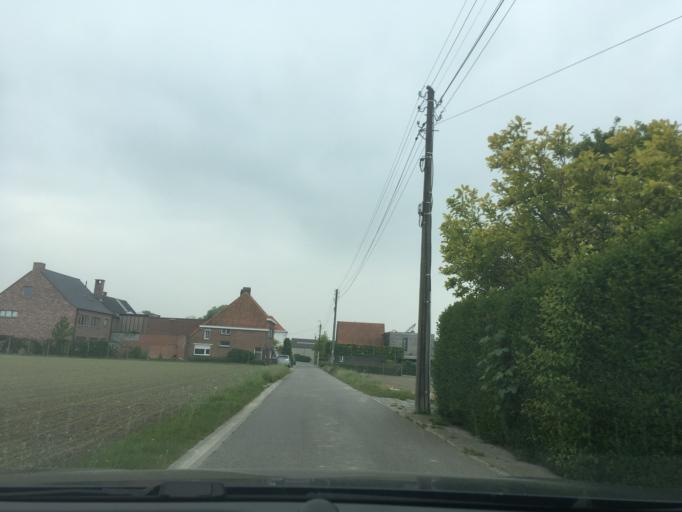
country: BE
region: Flanders
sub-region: Provincie West-Vlaanderen
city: Lichtervelde
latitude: 51.0023
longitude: 3.1349
